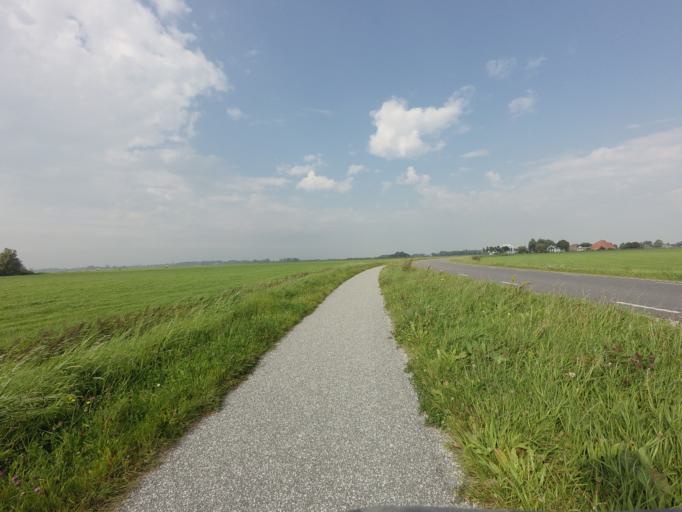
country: NL
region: Friesland
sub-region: Sudwest Fryslan
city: Bolsward
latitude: 53.0384
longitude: 5.5451
